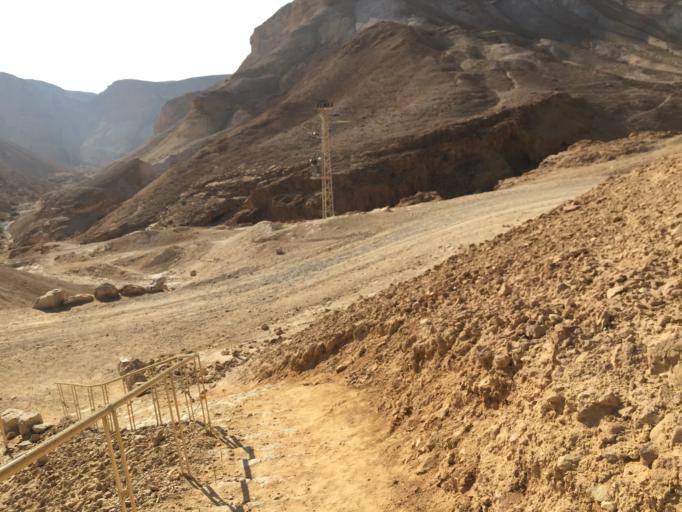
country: IL
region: Southern District
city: `En Boqeq
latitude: 31.3173
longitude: 35.3499
